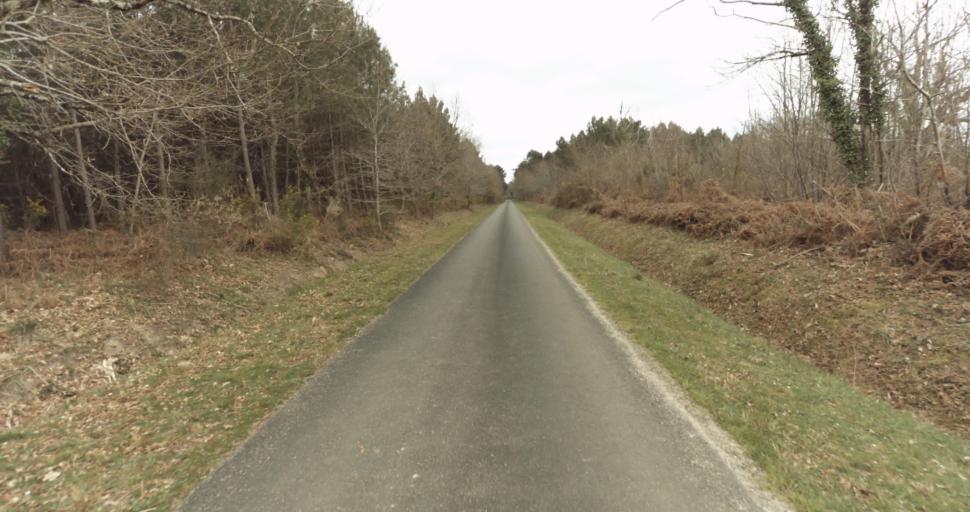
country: FR
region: Aquitaine
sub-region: Departement des Landes
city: Roquefort
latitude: 44.0651
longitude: -0.3874
